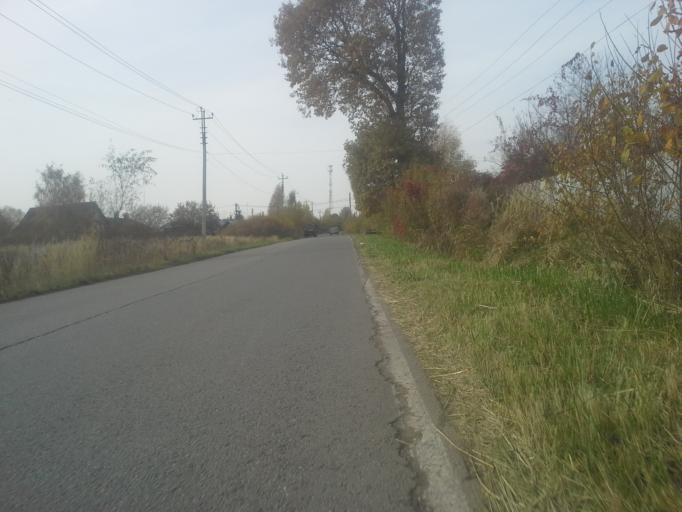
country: RU
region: Moskovskaya
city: Aprelevka
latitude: 55.5588
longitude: 37.0495
